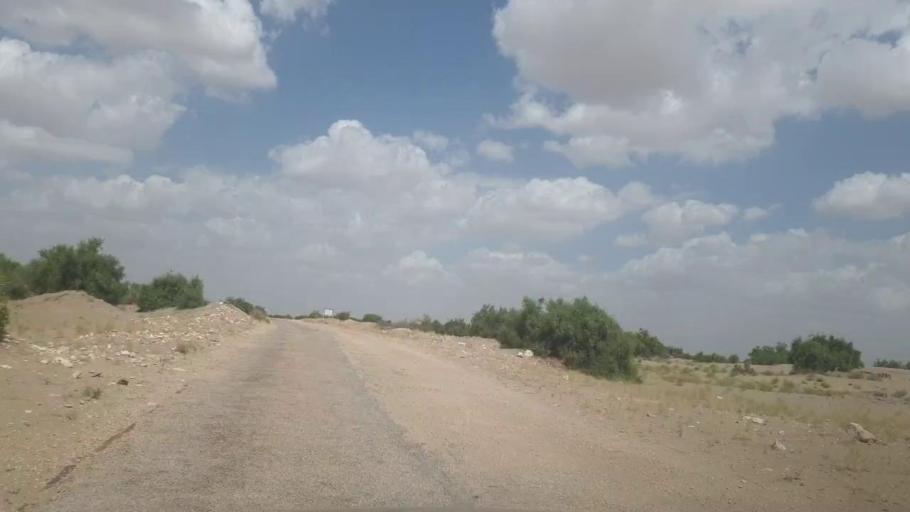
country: PK
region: Sindh
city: Kot Diji
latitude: 27.2678
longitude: 69.1812
